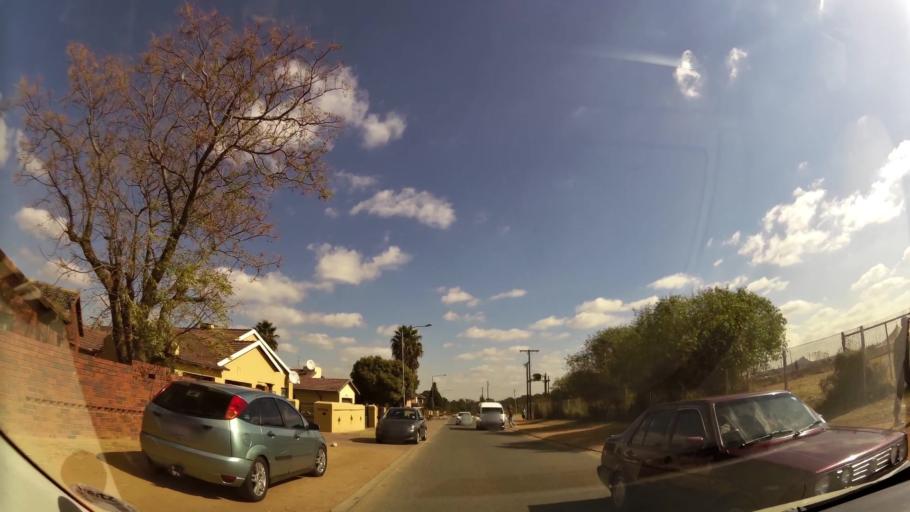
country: ZA
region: Gauteng
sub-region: West Rand District Municipality
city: Krugersdorp
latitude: -26.1487
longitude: 27.7855
